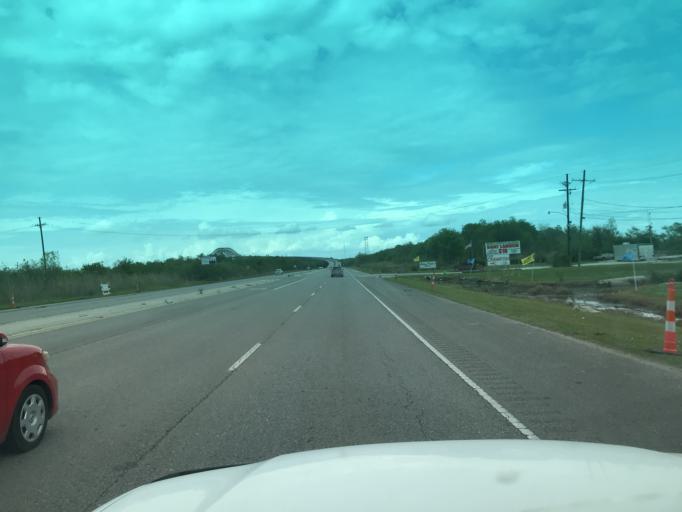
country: US
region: Louisiana
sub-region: Saint Bernard Parish
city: Chalmette
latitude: 29.9905
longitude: -89.9429
